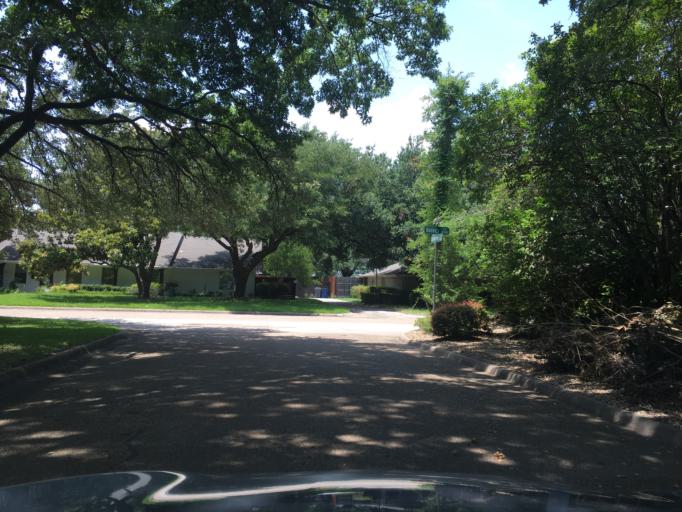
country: US
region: Texas
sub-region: Dallas County
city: Addison
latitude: 32.9127
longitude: -96.8140
